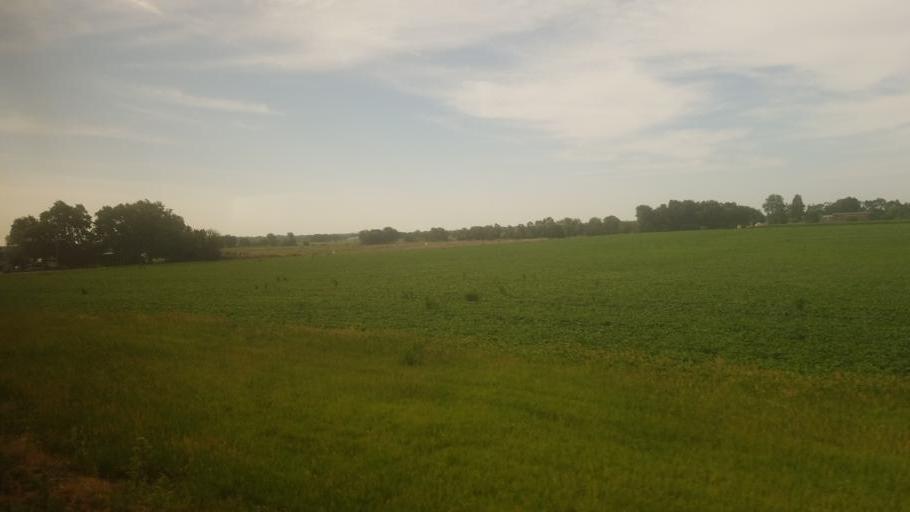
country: US
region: Kansas
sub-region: Douglas County
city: Eudora
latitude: 38.9499
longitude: -95.1603
